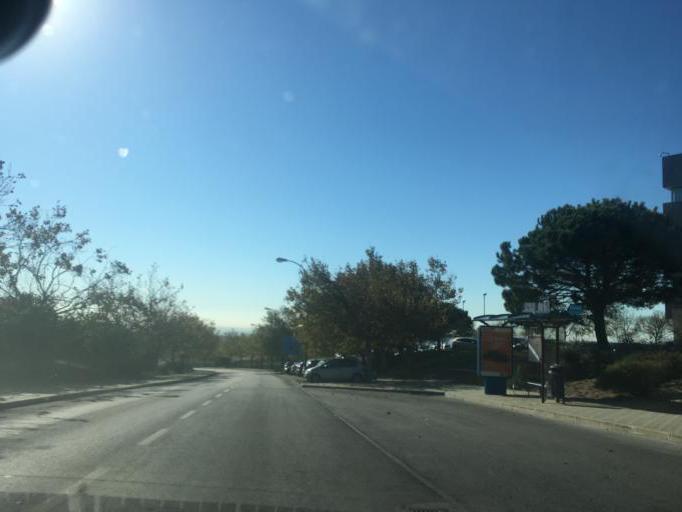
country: PT
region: Lisbon
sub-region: Oeiras
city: Porto Salvo
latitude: 38.7383
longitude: -9.3041
